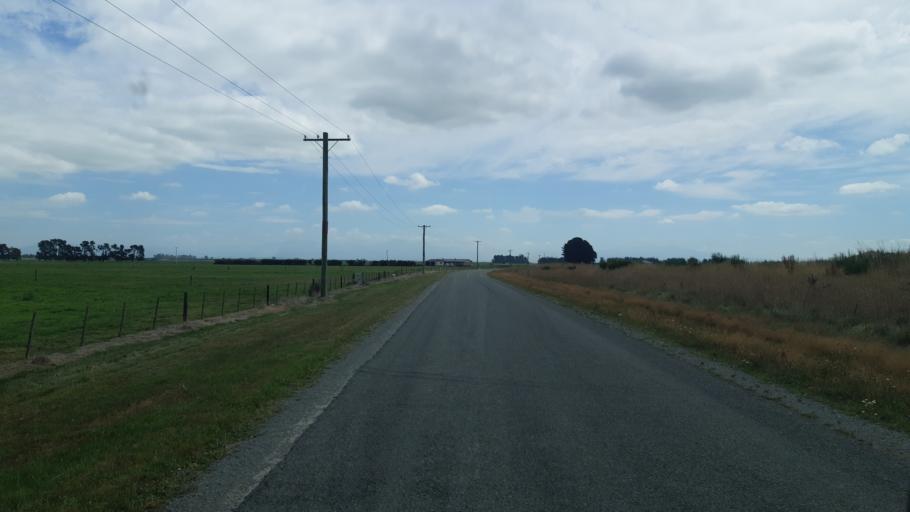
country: NZ
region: Canterbury
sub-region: Timaru District
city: Timaru
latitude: -44.1634
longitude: 171.4414
